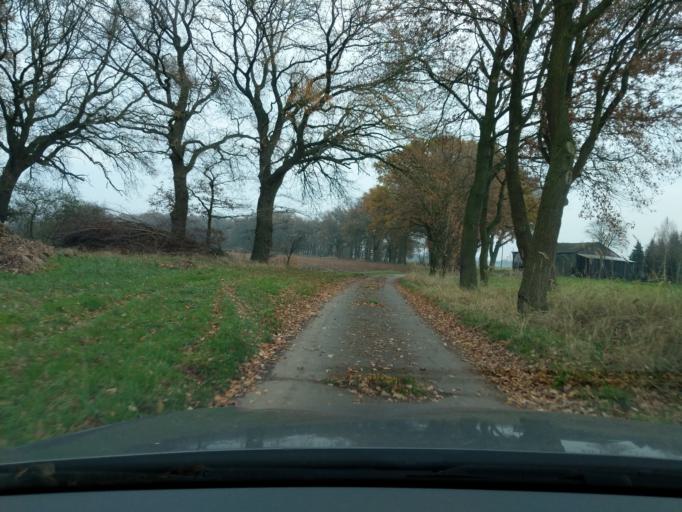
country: DE
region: Lower Saxony
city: Brietlingen
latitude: 53.3631
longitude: 10.4552
